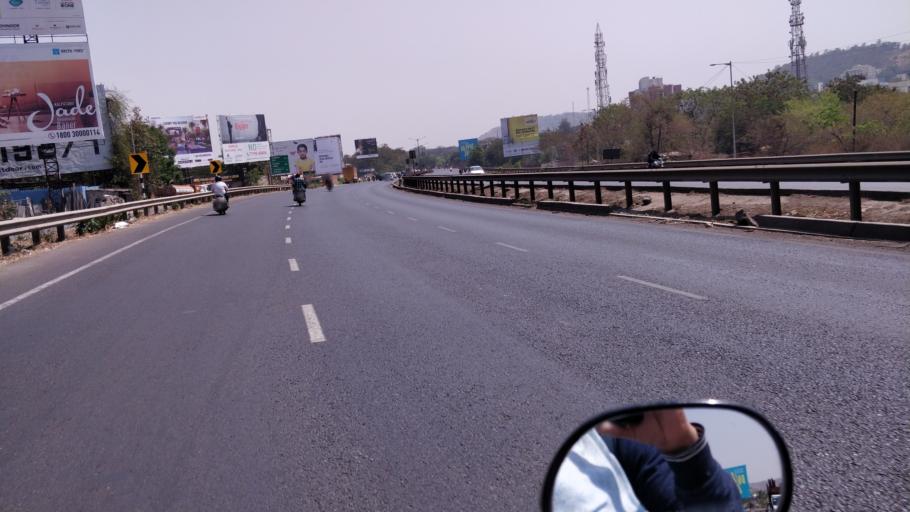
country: IN
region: Maharashtra
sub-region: Pune Division
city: Shivaji Nagar
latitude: 18.5260
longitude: 73.7729
